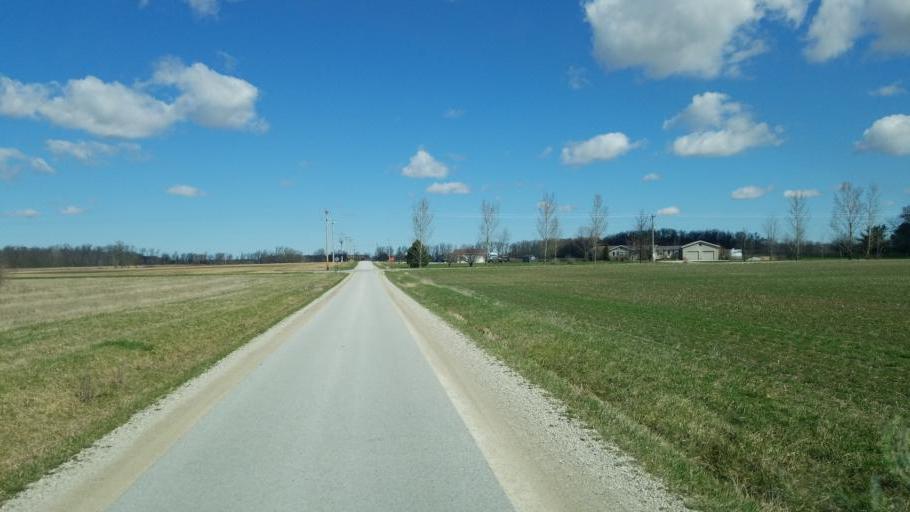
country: US
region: Ohio
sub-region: Sandusky County
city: Mount Carmel
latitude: 41.2111
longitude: -82.9373
